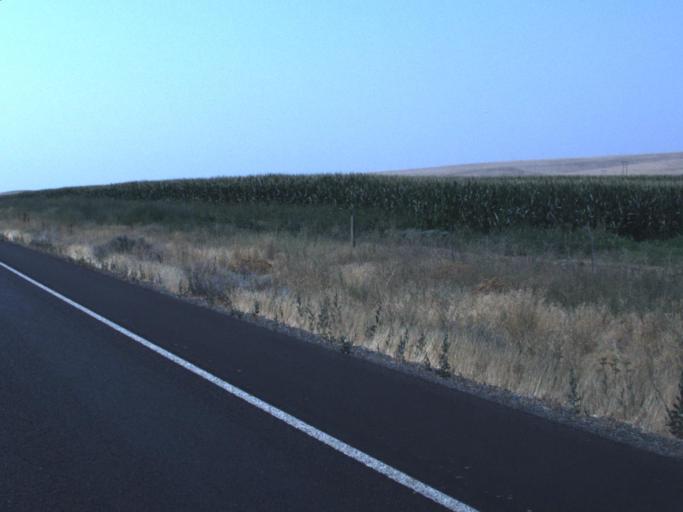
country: US
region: Washington
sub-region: Yakima County
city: Sunnyside
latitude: 46.5102
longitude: -120.0648
